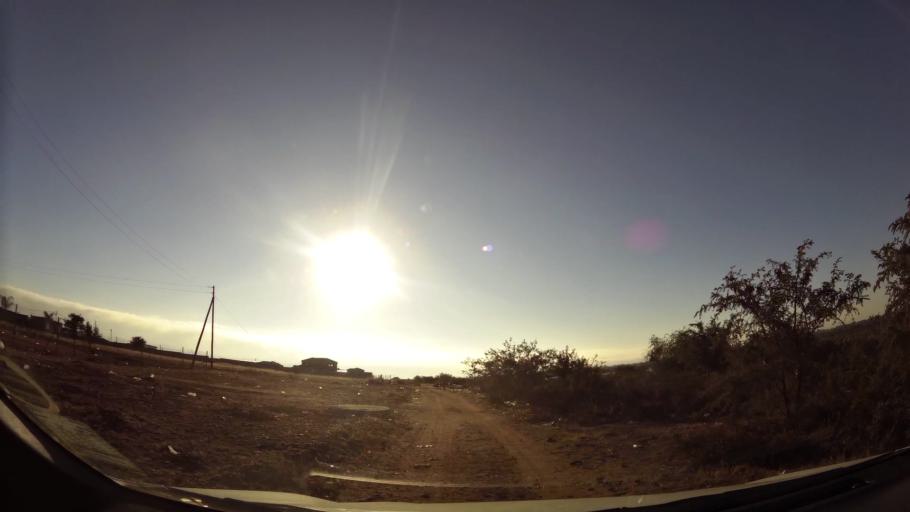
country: ZA
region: Limpopo
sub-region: Capricorn District Municipality
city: Polokwane
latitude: -23.8411
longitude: 29.3647
